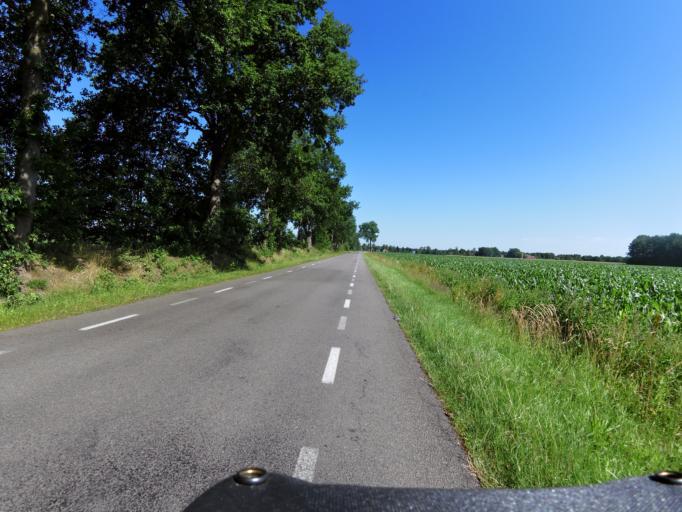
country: NL
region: Overijssel
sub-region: Gemeente Twenterand
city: Den Ham
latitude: 52.5310
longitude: 6.4456
